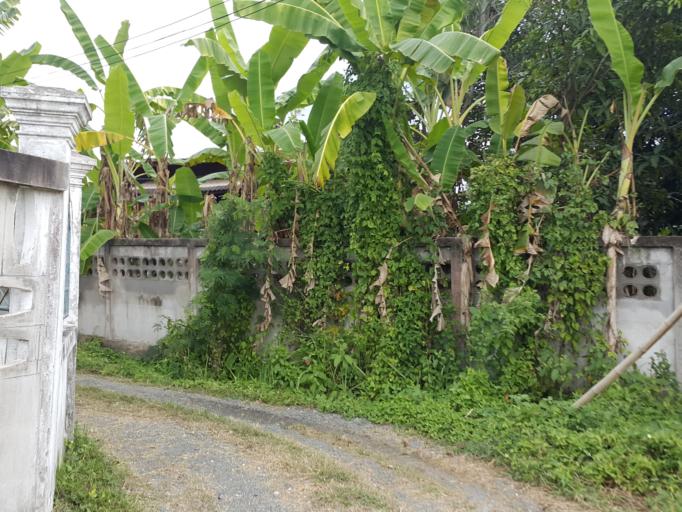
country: TH
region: Chiang Mai
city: San Sai
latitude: 18.8670
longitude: 99.1119
